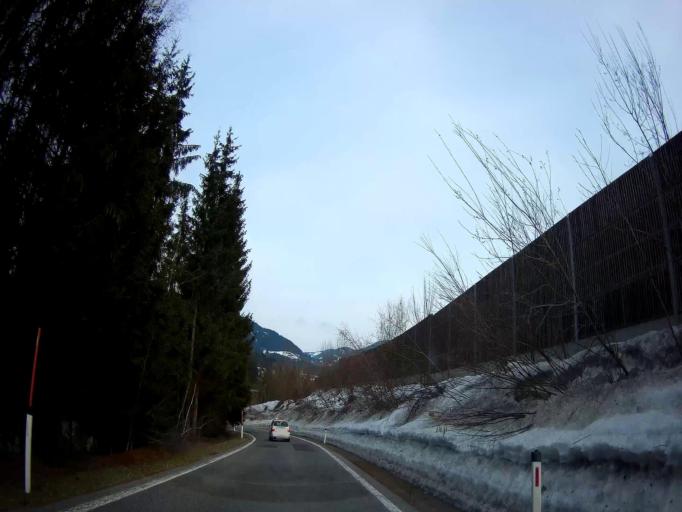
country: AT
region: Salzburg
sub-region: Politischer Bezirk Sankt Johann im Pongau
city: Huttau
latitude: 47.4258
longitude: 13.3435
